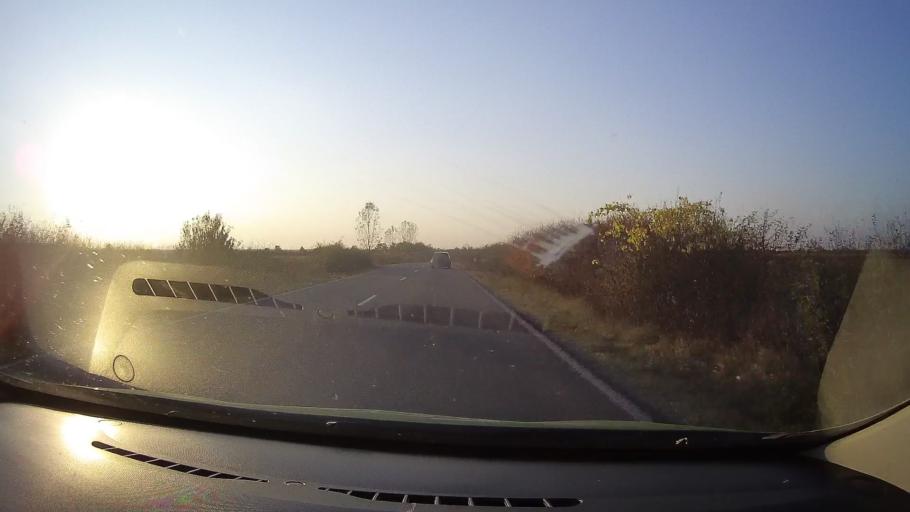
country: RO
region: Arad
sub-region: Comuna Barsa
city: Barsa
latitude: 46.4048
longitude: 22.0233
